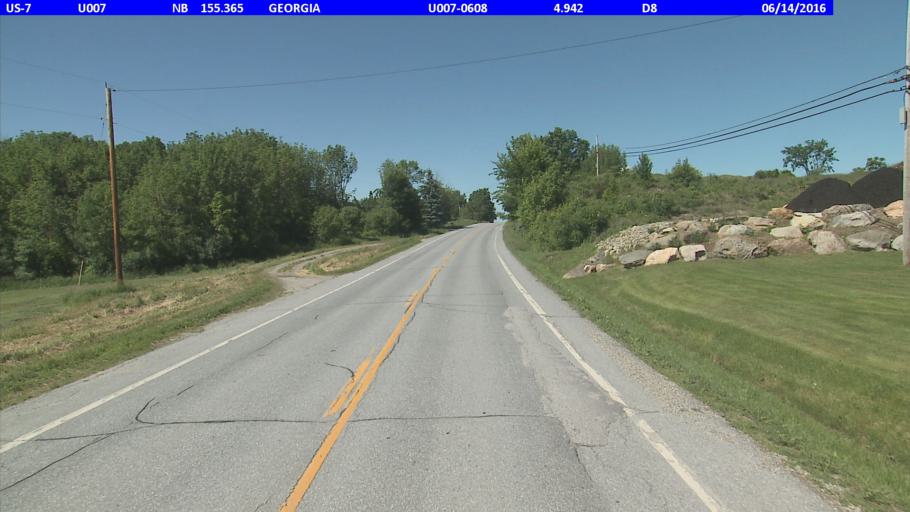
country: US
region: Vermont
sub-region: Franklin County
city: Saint Albans
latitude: 44.7424
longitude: -73.1144
